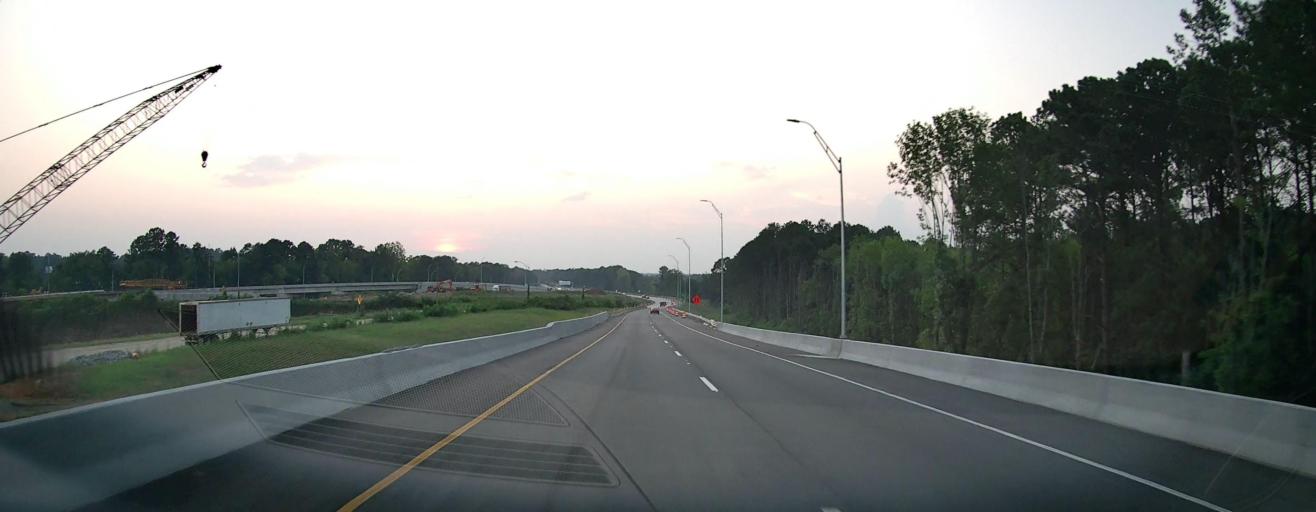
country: US
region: Georgia
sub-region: Bibb County
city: Macon
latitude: 32.8573
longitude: -83.6385
